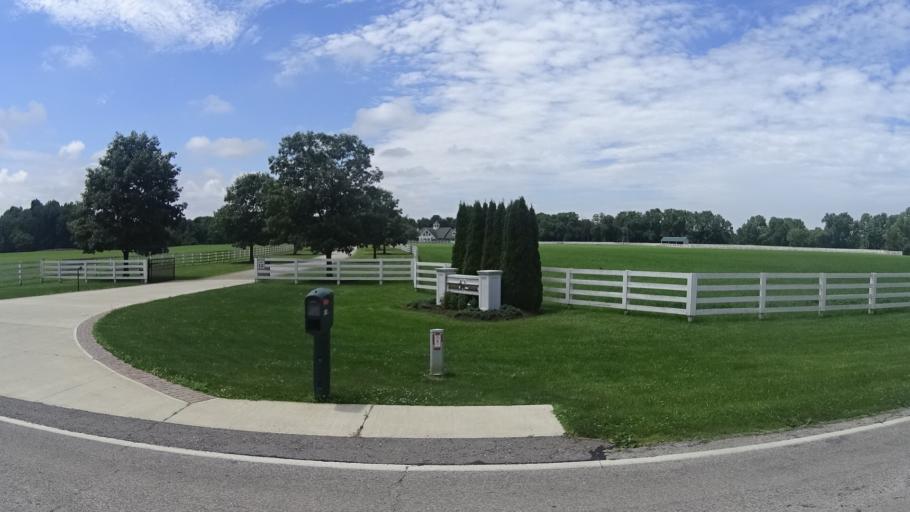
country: US
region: Ohio
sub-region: Erie County
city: Milan
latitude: 41.3072
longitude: -82.5840
